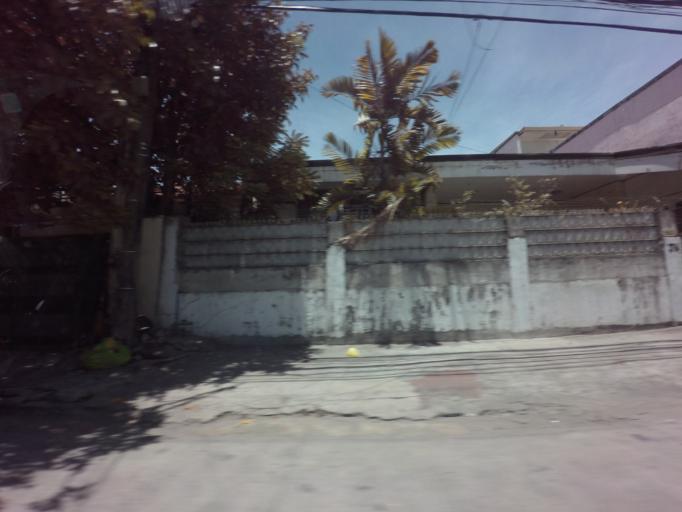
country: PH
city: Sambayanihan People's Village
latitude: 14.4912
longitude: 121.0369
